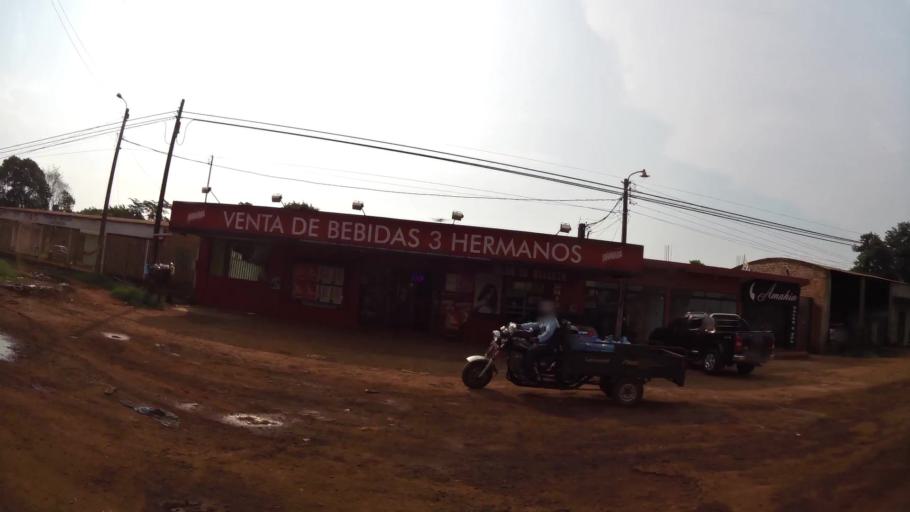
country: PY
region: Alto Parana
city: Ciudad del Este
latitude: -25.4837
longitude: -54.6596
